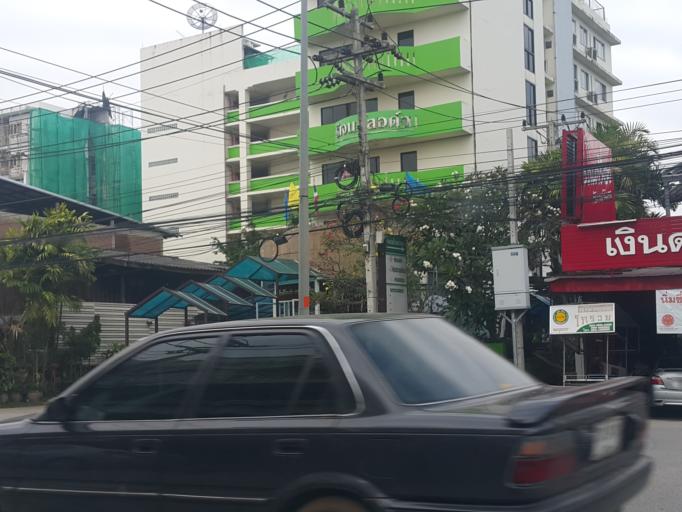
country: TH
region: Lampang
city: Lampang
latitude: 18.2911
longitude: 99.5124
